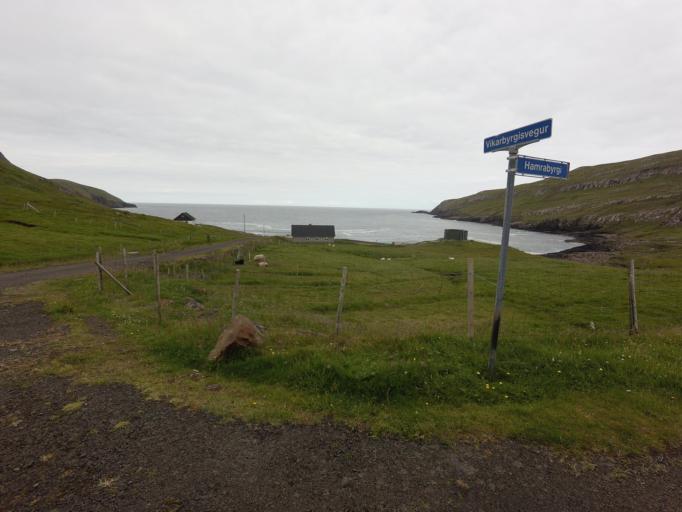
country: FO
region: Suduroy
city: Vagur
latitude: 61.4422
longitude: -6.7256
